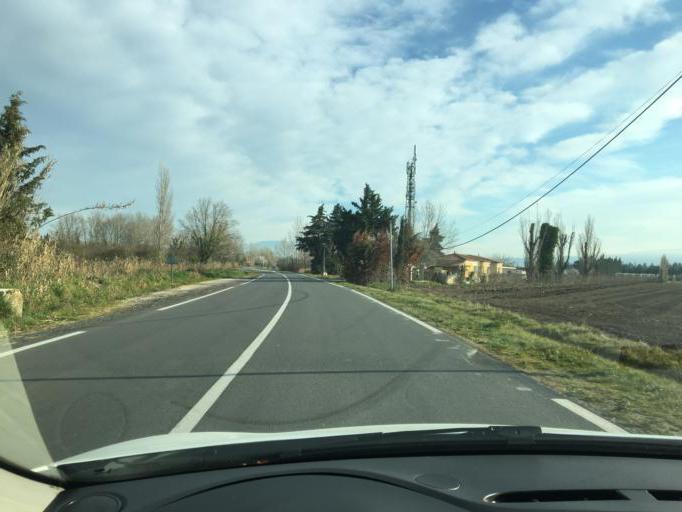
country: FR
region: Provence-Alpes-Cote d'Azur
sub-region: Departement du Vaucluse
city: Le Thor
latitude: 43.9200
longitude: 4.9828
